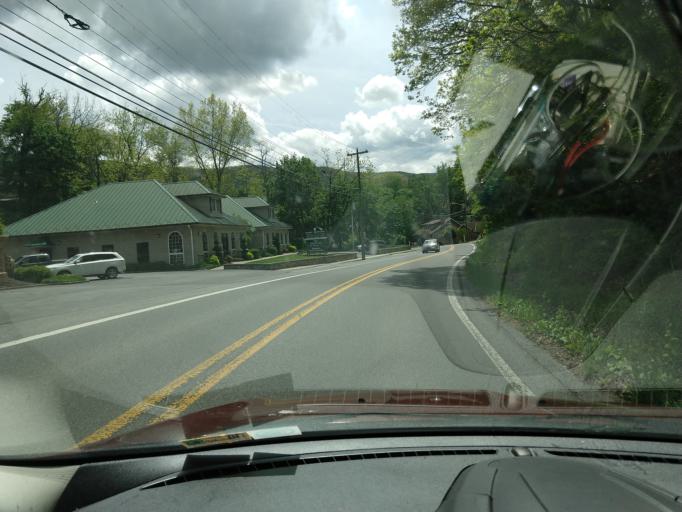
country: US
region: West Virginia
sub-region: Mercer County
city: Bluefield
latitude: 37.2532
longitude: -81.2319
